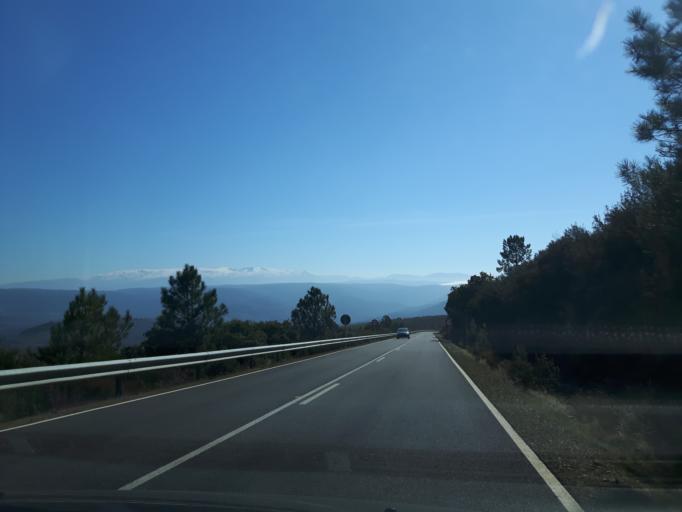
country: ES
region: Castille and Leon
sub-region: Provincia de Salamanca
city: Sotoserrano
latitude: 40.4404
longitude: -6.0468
